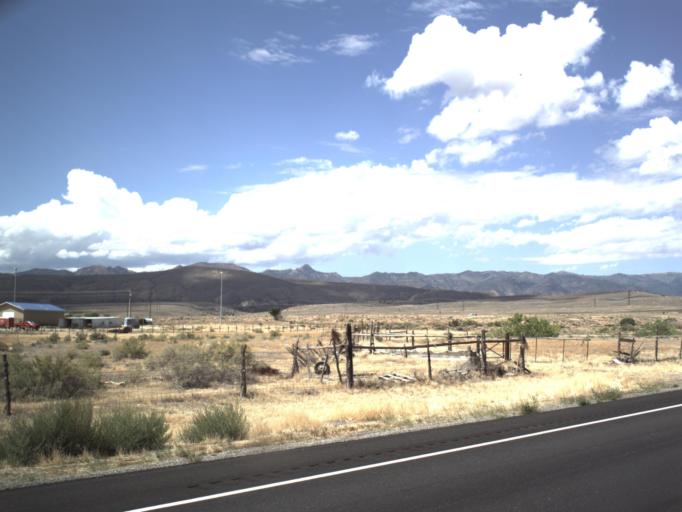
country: US
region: Utah
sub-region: Sevier County
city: Aurora
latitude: 38.9567
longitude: -111.9200
